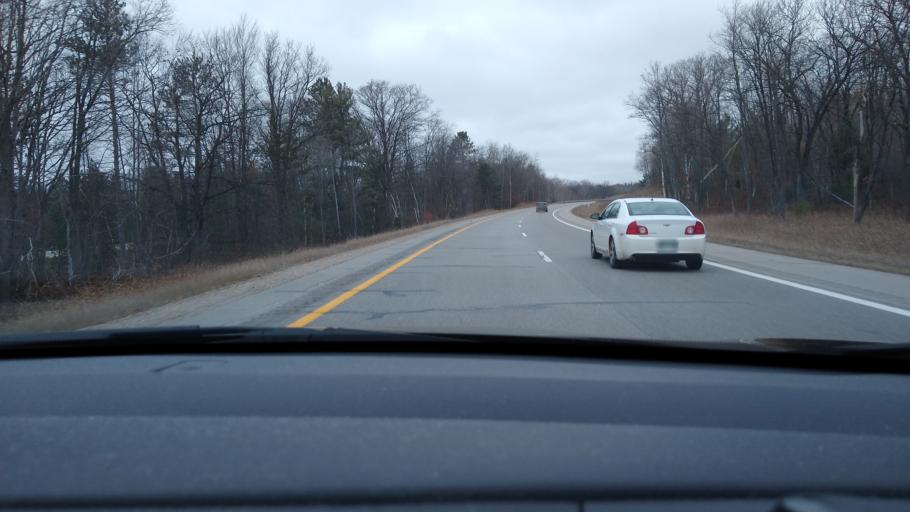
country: US
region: Michigan
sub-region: Otsego County
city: Gaylord
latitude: 44.9065
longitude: -84.6917
